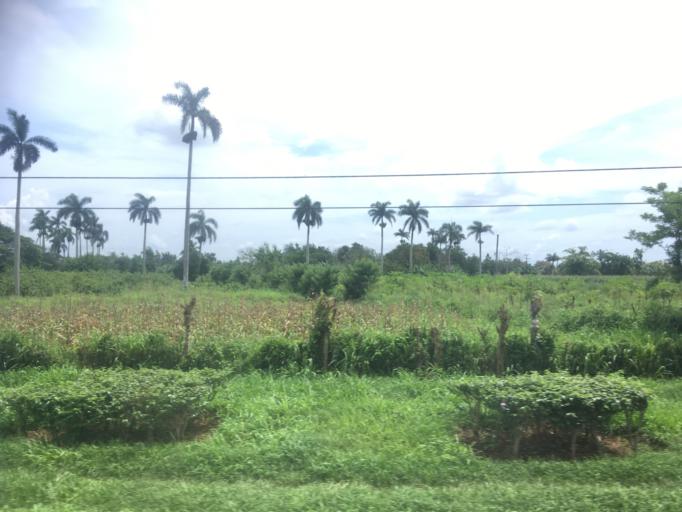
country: CU
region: Matanzas
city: Perico
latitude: 22.7757
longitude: -81.0322
